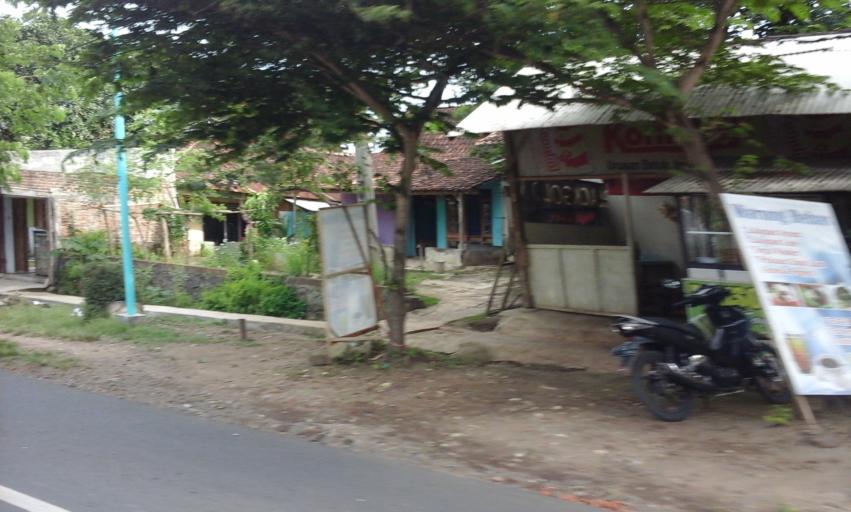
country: ID
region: East Java
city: Olehsari
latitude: -8.2159
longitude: 114.3207
